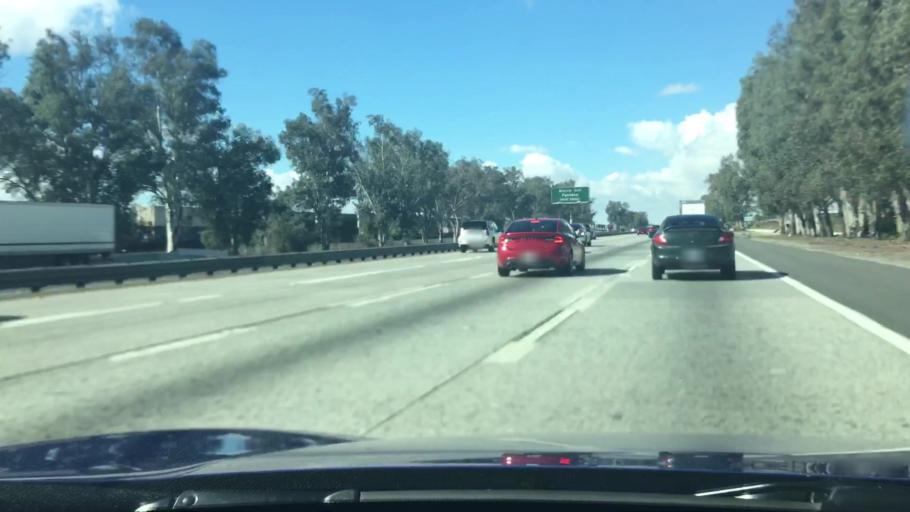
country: US
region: California
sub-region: San Bernardino County
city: Bloomington
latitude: 34.0677
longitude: -117.4182
